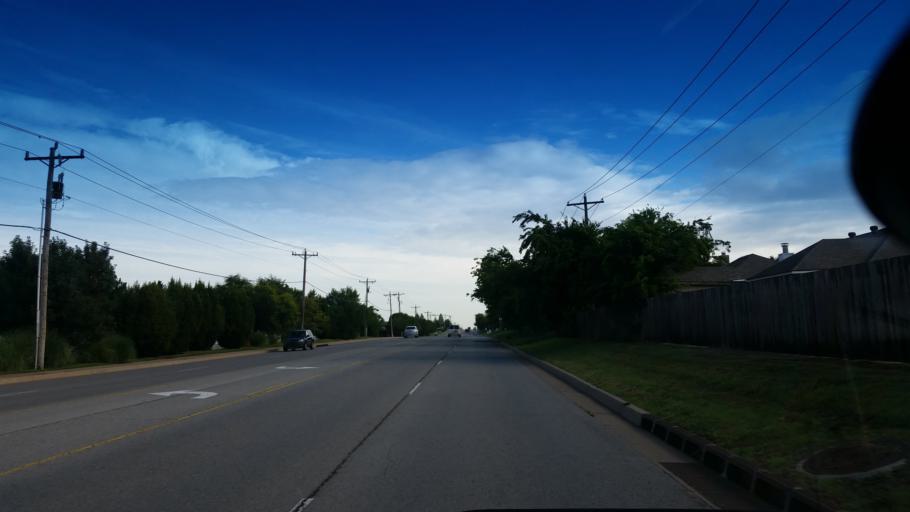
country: US
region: Oklahoma
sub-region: Oklahoma County
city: Edmond
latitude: 35.6275
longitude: -97.5137
